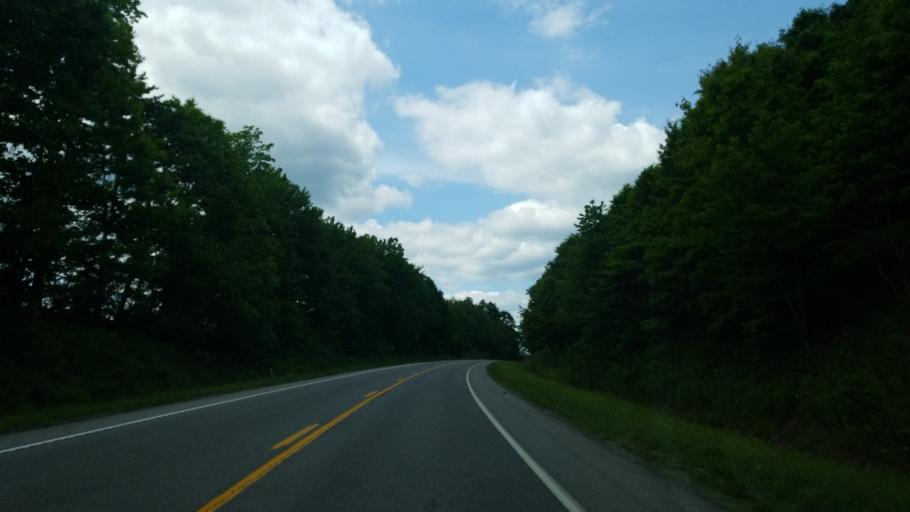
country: US
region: Pennsylvania
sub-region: Clearfield County
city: Hyde
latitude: 40.9202
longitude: -78.3838
